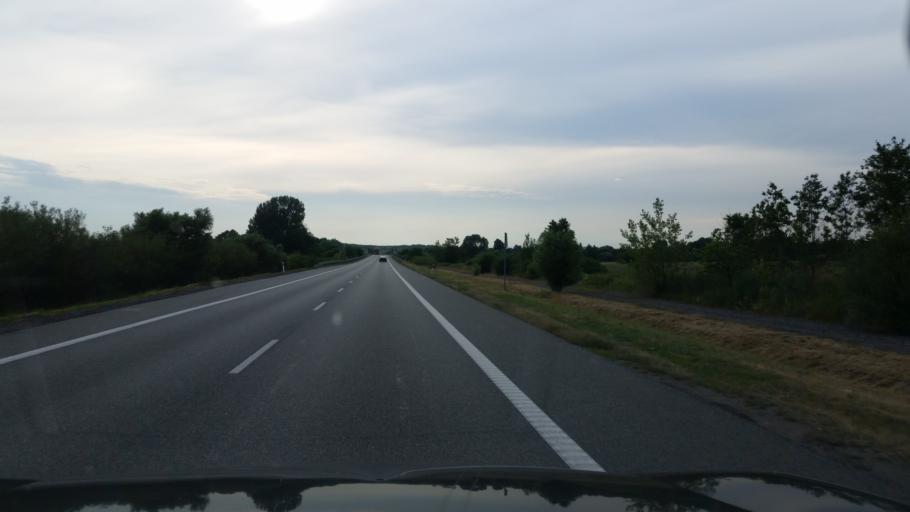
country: PL
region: Silesian Voivodeship
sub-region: Powiat bedzinski
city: Sarnow
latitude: 50.4222
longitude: 19.1853
